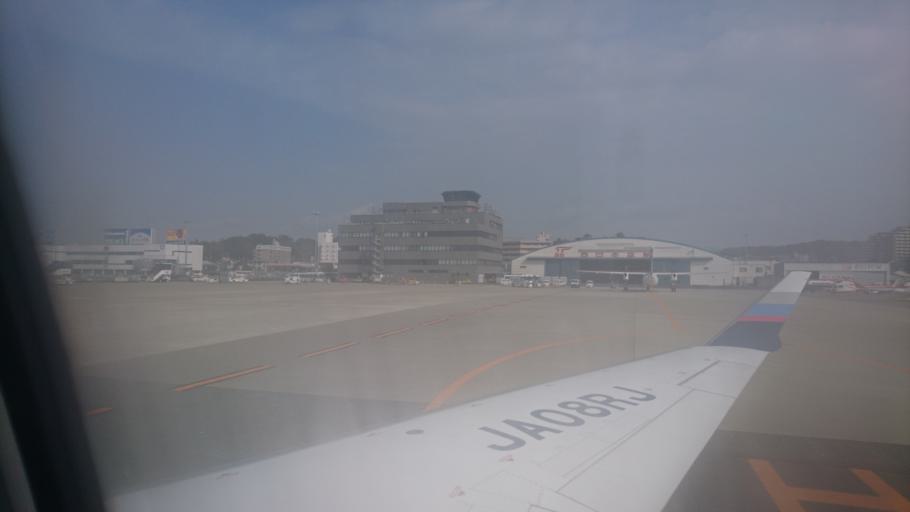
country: JP
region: Fukuoka
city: Fukuoka-shi
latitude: 33.5925
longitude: 130.4485
